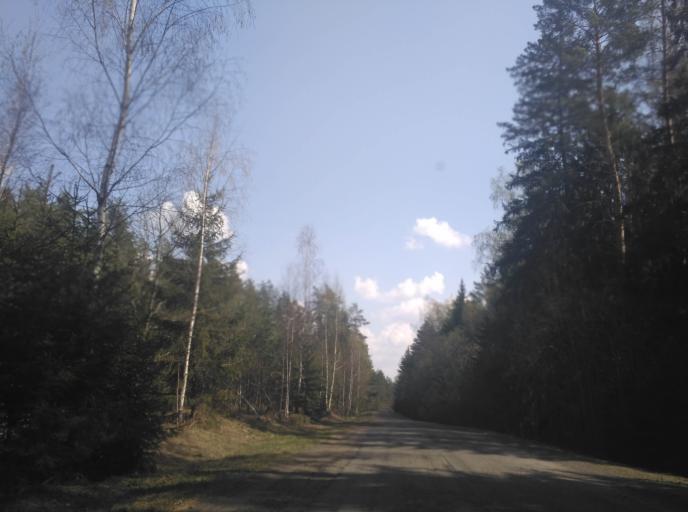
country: BY
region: Minsk
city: Loshnitsa
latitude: 54.4938
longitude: 28.7061
